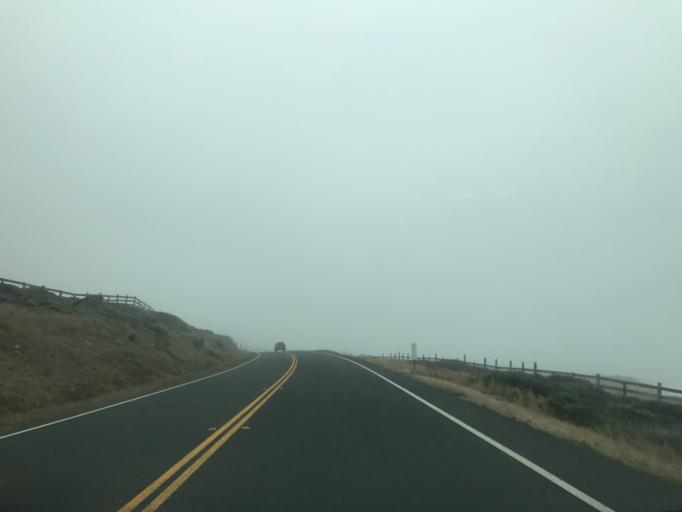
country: US
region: California
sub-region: Sonoma County
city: Sea Ranch
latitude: 38.6309
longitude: -123.3861
